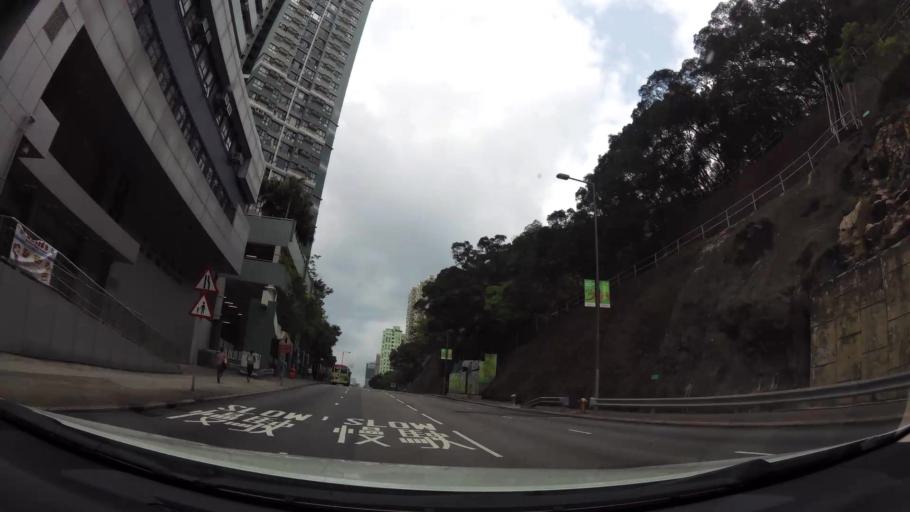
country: HK
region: Kowloon City
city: Kowloon
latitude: 22.3219
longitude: 114.2247
